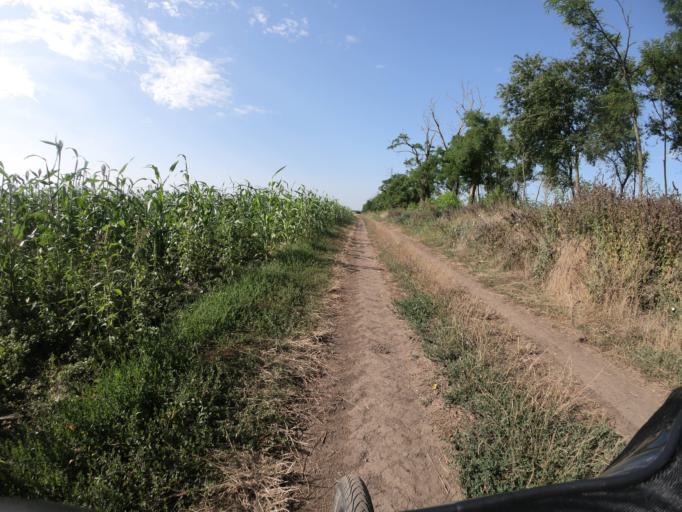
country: HU
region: Hajdu-Bihar
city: Egyek
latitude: 47.6034
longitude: 20.9800
